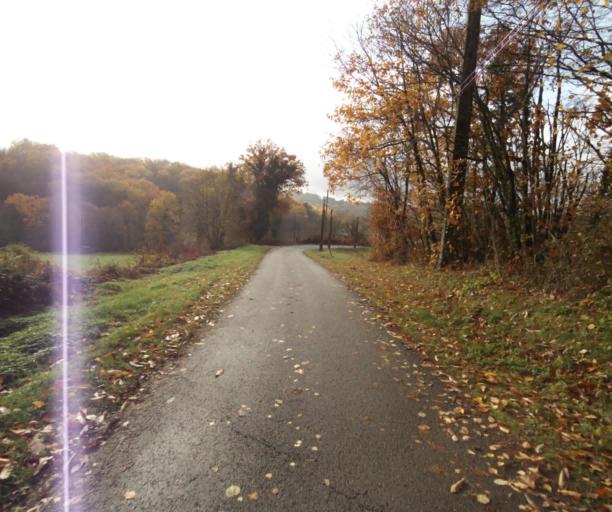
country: FR
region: Limousin
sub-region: Departement de la Correze
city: Sainte-Fereole
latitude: 45.2115
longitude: 1.6342
